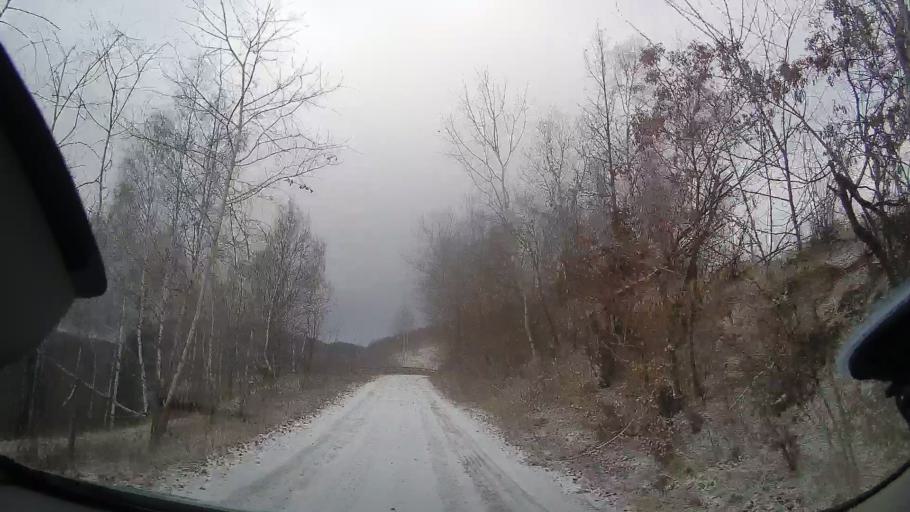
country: RO
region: Cluj
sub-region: Comuna Valea Ierii
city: Valea Ierii
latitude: 46.6559
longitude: 23.3488
